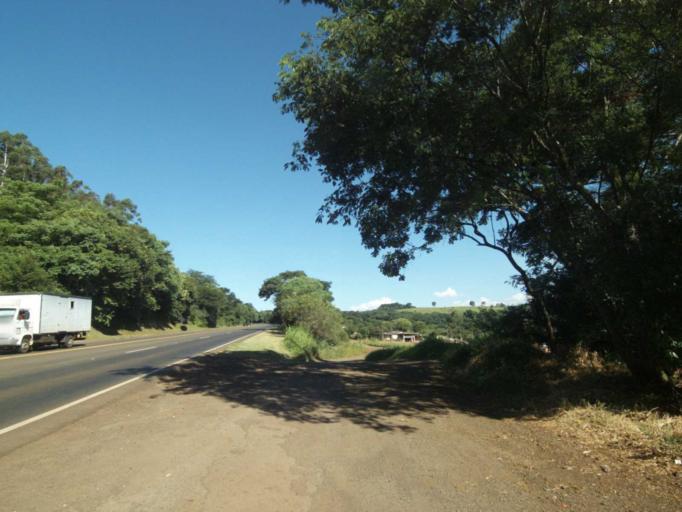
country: BR
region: Parana
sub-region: Laranjeiras Do Sul
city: Laranjeiras do Sul
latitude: -25.3784
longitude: -52.1973
